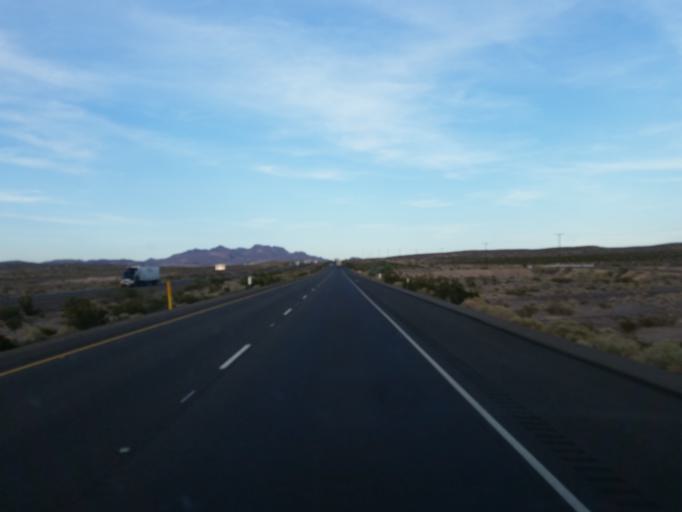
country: US
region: California
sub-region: San Bernardino County
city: Fort Irwin
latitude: 34.7859
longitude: -116.4362
